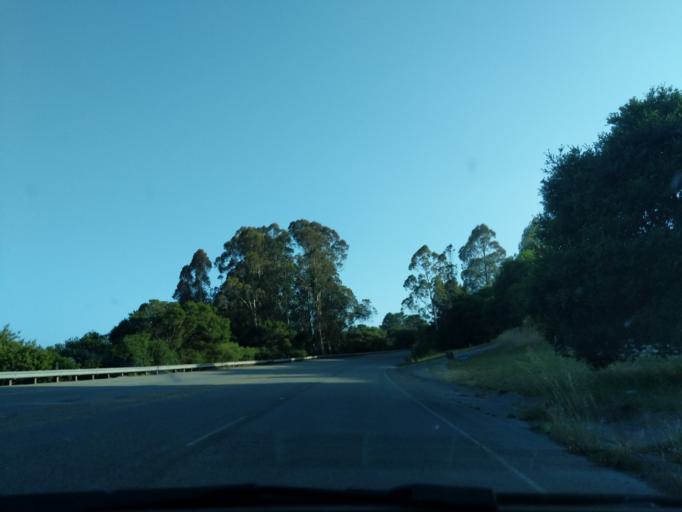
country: US
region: California
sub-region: Monterey County
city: Las Lomas
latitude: 36.8806
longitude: -121.7477
